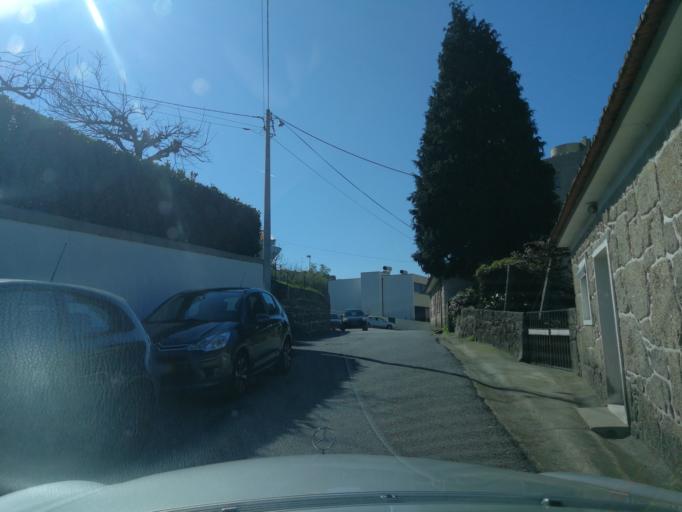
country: PT
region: Braga
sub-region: Vila Nova de Famalicao
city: Vila Nova de Famalicao
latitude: 41.4000
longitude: -8.5134
